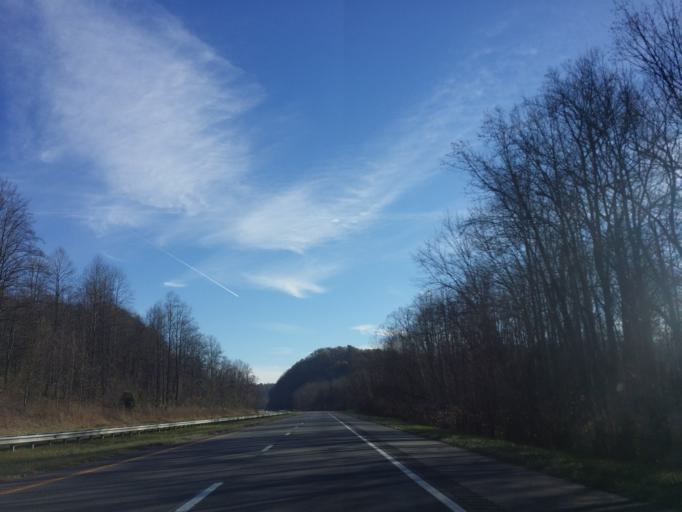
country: US
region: North Carolina
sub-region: McDowell County
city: West Marion
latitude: 35.6393
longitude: -82.1345
